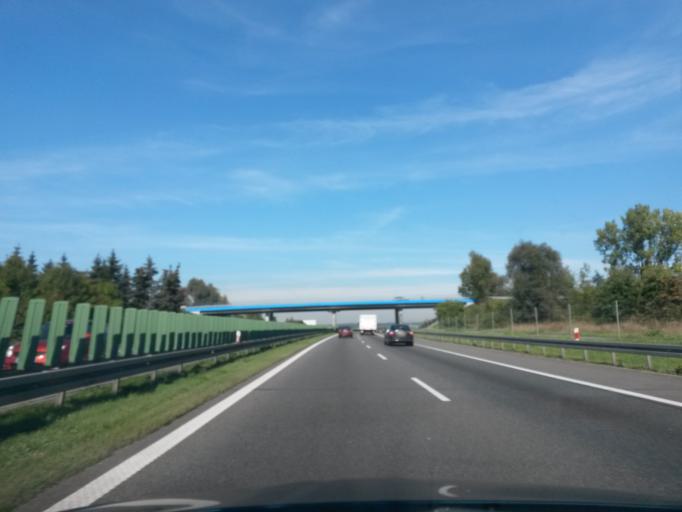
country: PL
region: Lesser Poland Voivodeship
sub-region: Powiat krakowski
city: Kryspinow
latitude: 50.0600
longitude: 19.8096
